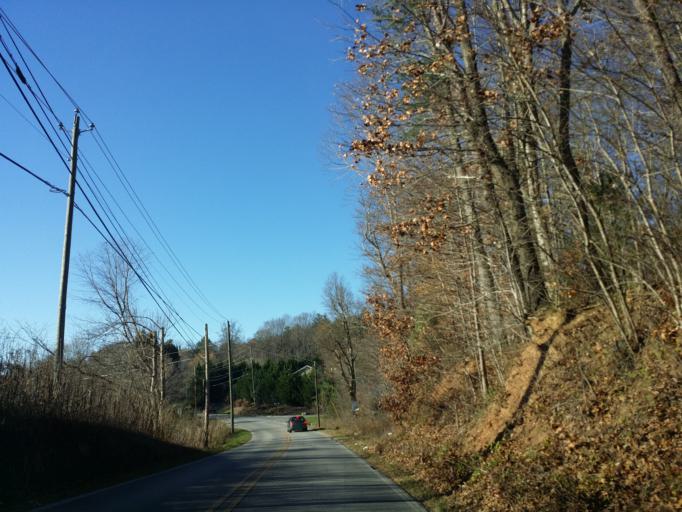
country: US
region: North Carolina
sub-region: Buncombe County
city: Swannanoa
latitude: 35.6056
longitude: -82.4094
